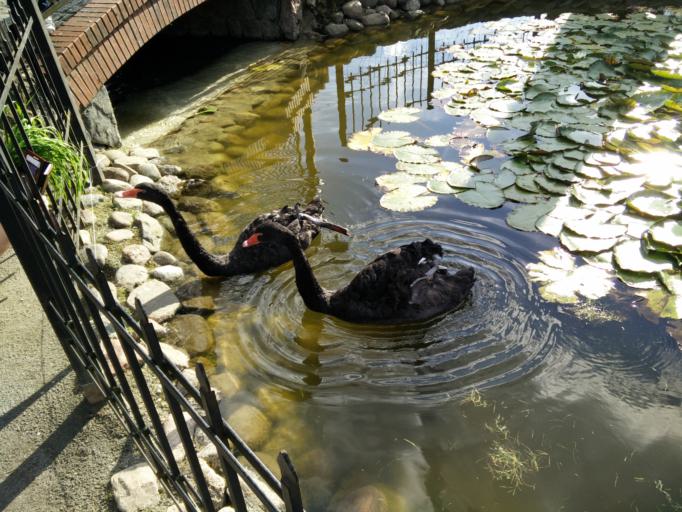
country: LT
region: Vilnius County
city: Rasos
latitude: 54.6839
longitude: 25.3578
